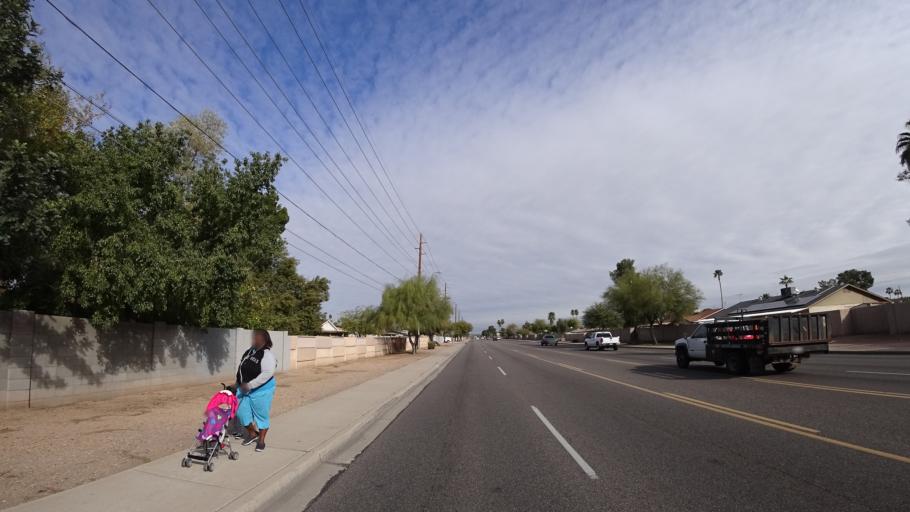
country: US
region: Arizona
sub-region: Maricopa County
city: Glendale
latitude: 33.5904
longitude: -112.1516
